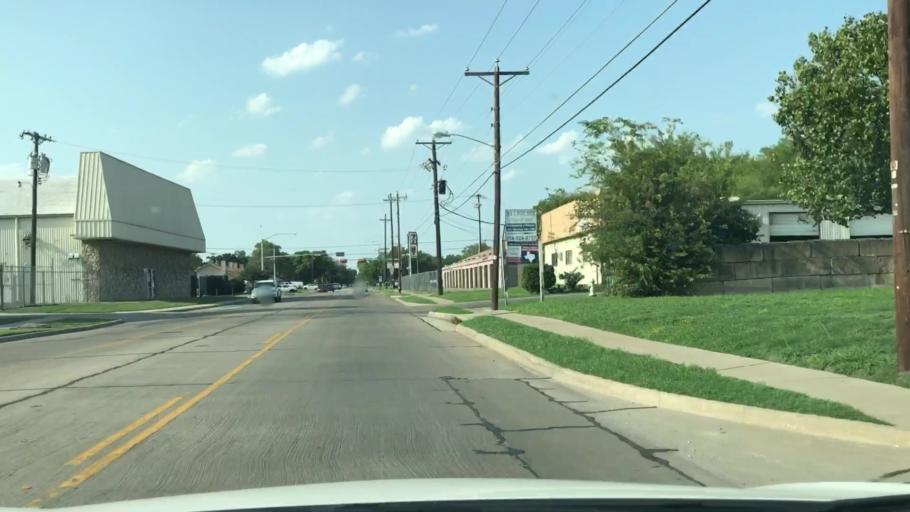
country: US
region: Texas
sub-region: Dallas County
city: Irving
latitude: 32.8162
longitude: -96.9343
